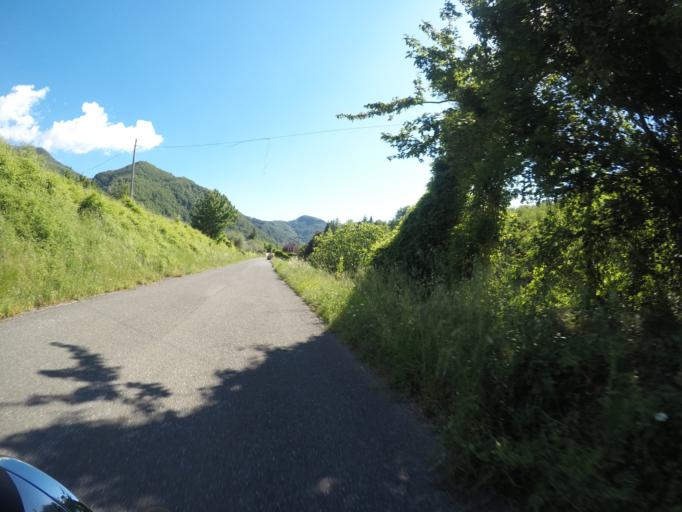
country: IT
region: Tuscany
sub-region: Provincia di Massa-Carrara
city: Fosdinovo
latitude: 44.1476
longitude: 10.0998
